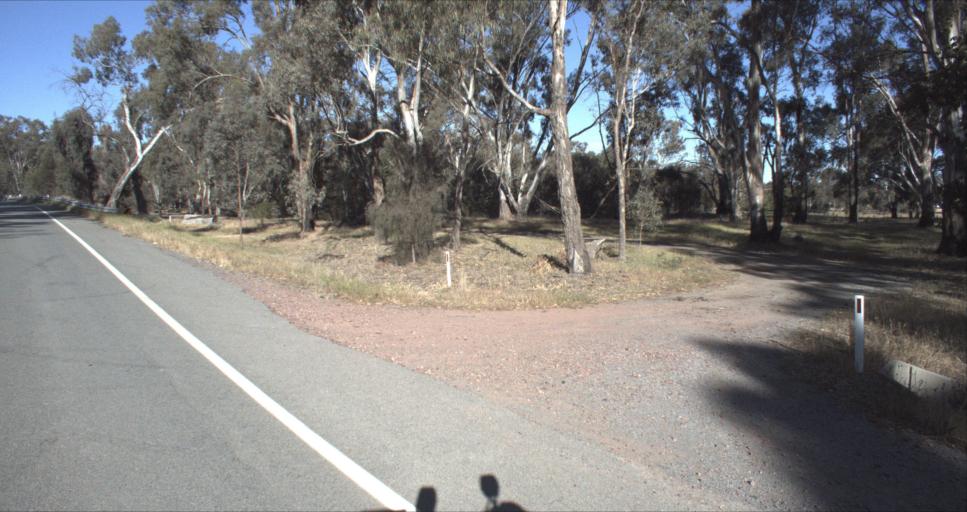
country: AU
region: New South Wales
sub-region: Leeton
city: Leeton
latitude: -34.6396
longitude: 146.3723
